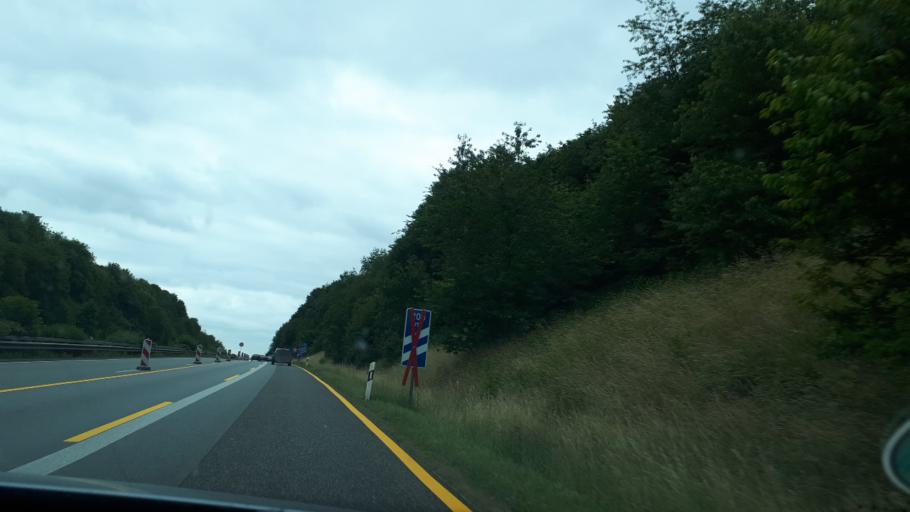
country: DE
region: Rheinland-Pfalz
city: Kaifenheim
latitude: 50.2500
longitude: 7.2165
